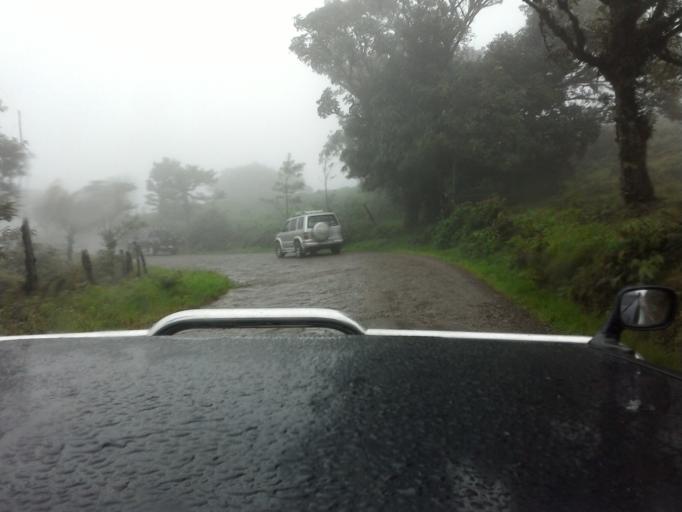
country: CR
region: Guanacaste
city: Juntas
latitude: 10.3431
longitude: -84.8015
